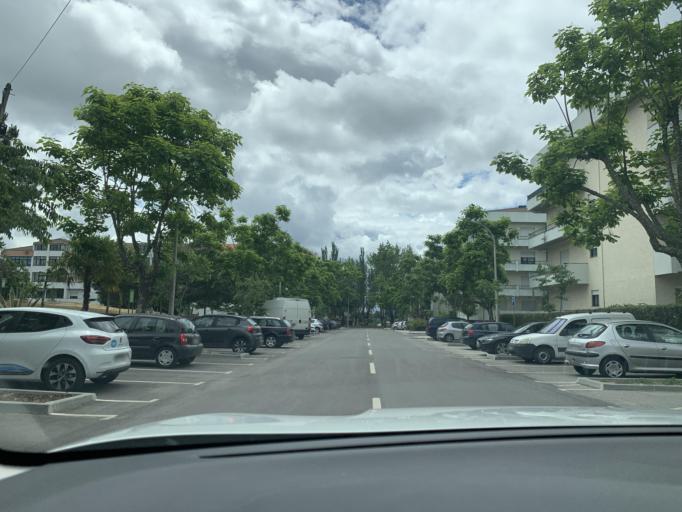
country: PT
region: Viseu
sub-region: Viseu
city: Rio de Loba
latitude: 40.6496
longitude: -7.8902
